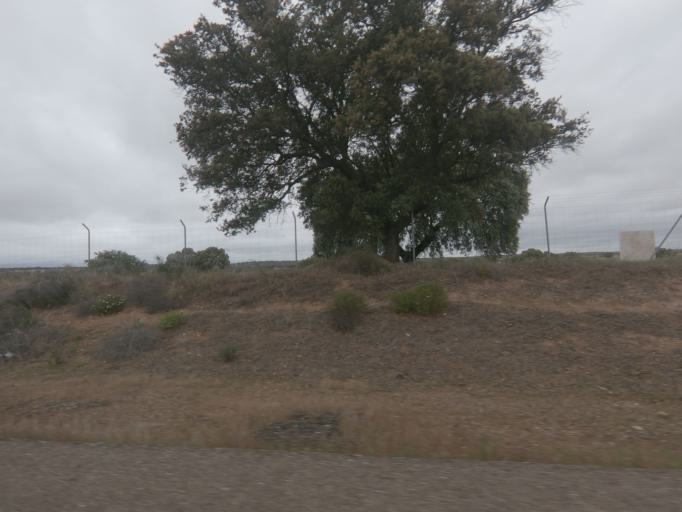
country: ES
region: Extremadura
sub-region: Provincia de Badajoz
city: Villar del Rey
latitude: 39.0163
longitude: -6.8510
